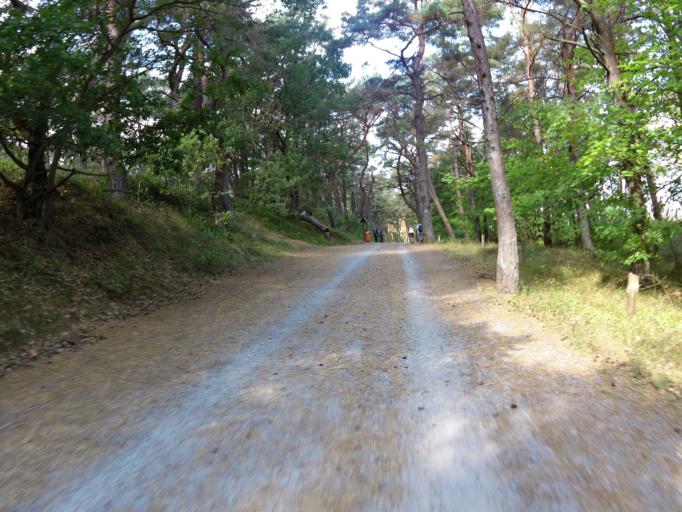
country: DE
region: Mecklenburg-Vorpommern
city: Ostseebad Zinnowitz
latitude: 54.0934
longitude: 13.8851
